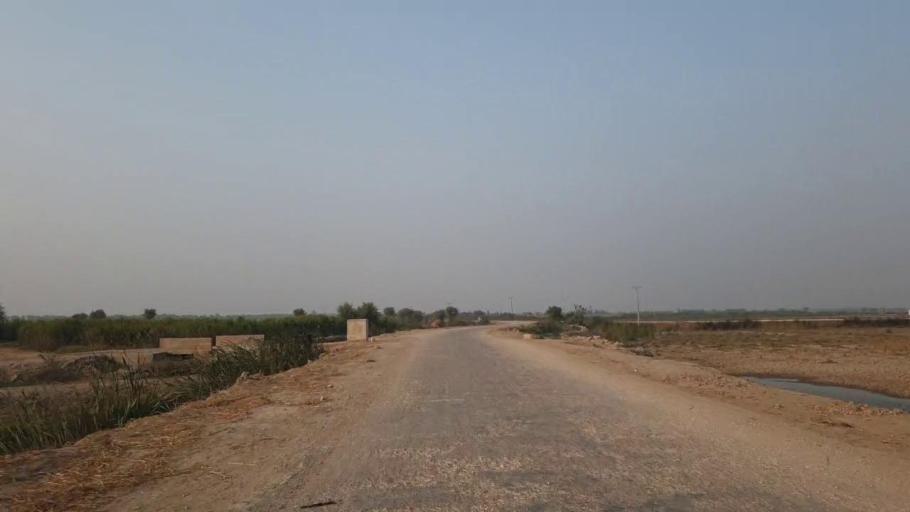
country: PK
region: Sindh
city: Tando Muhammad Khan
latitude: 25.1025
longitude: 68.4308
